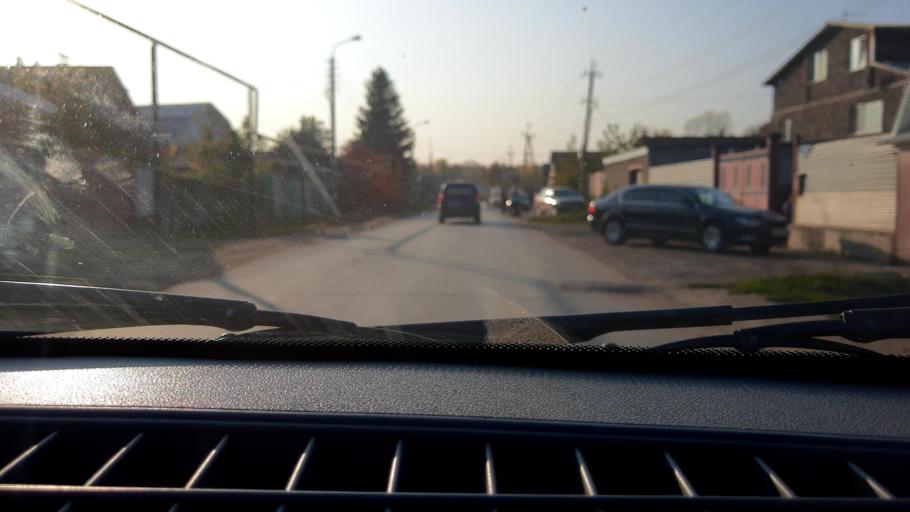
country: RU
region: Bashkortostan
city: Ufa
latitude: 54.6941
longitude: 55.9502
